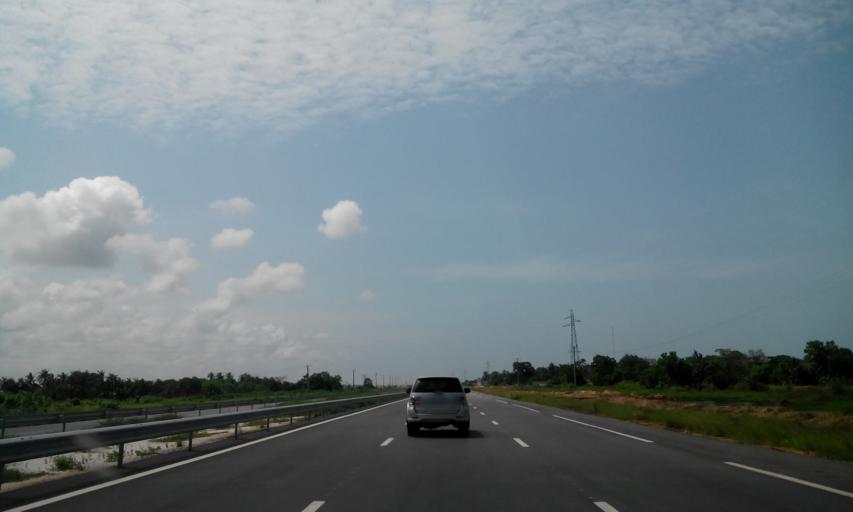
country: CI
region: Sud-Comoe
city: Grand-Bassam
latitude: 5.2333
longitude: -3.7650
